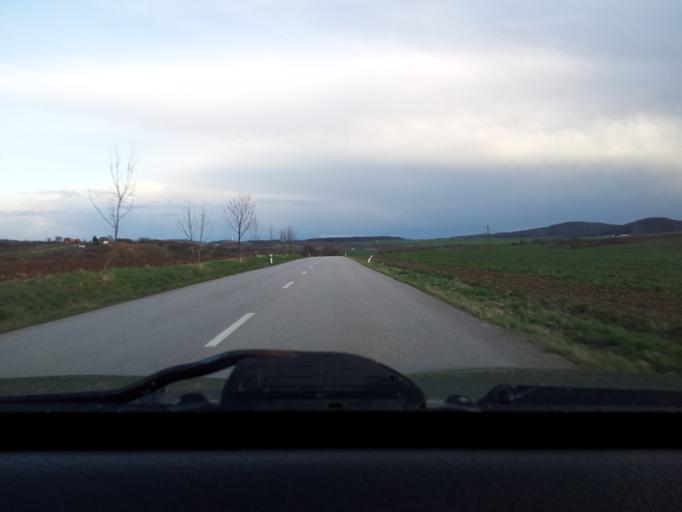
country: SK
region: Nitriansky
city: Tlmace
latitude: 48.3319
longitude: 18.4942
